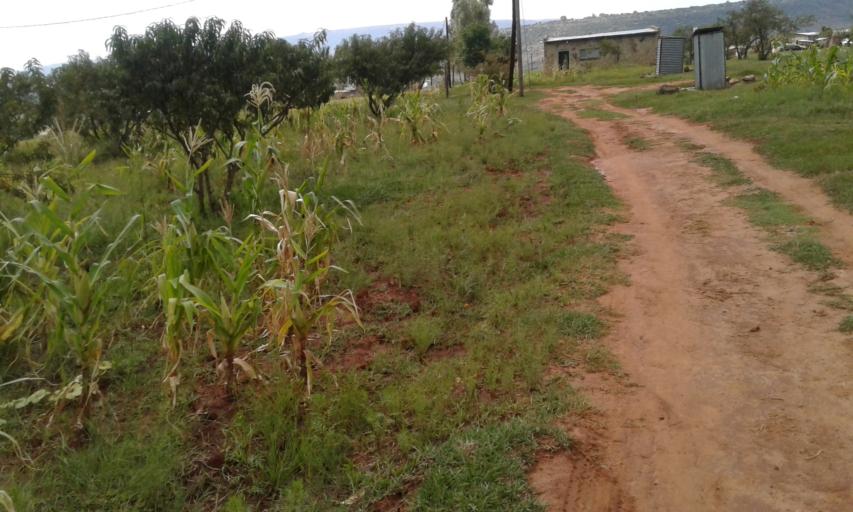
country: LS
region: Maseru
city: Maseru
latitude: -29.4237
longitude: 27.5717
